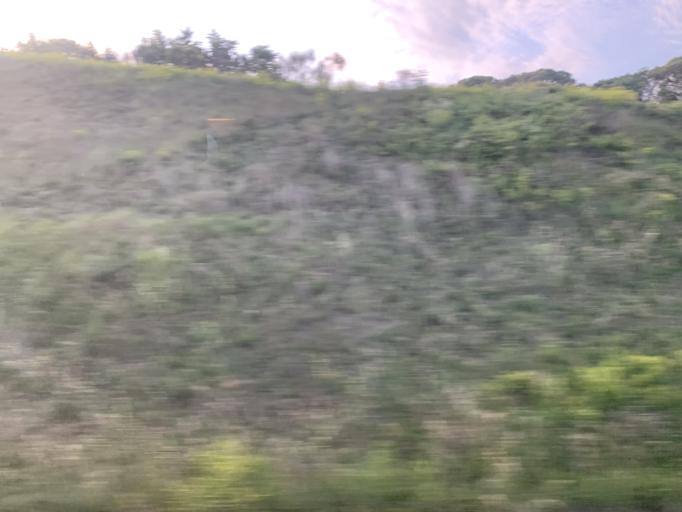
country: ES
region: Catalonia
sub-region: Provincia de Girona
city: Hostalric
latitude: 41.7520
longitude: 2.6476
